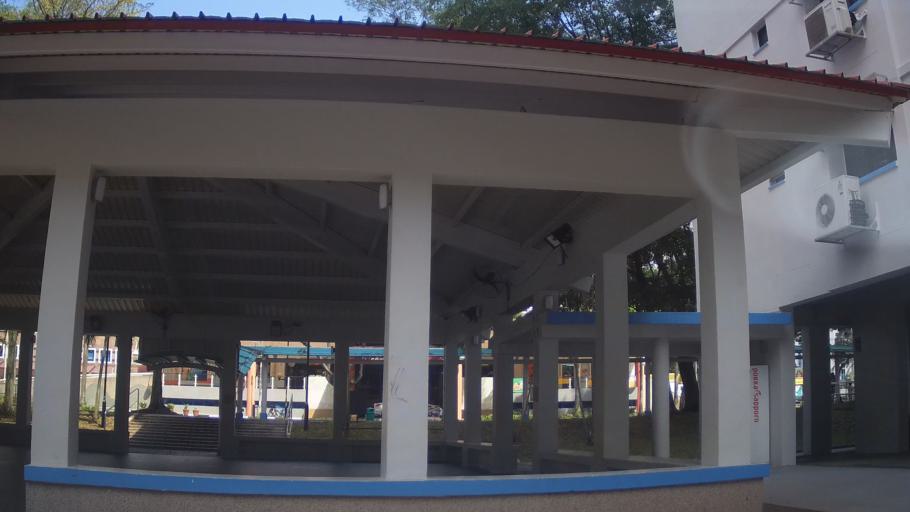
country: MY
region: Johor
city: Johor Bahru
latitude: 1.3845
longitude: 103.7668
